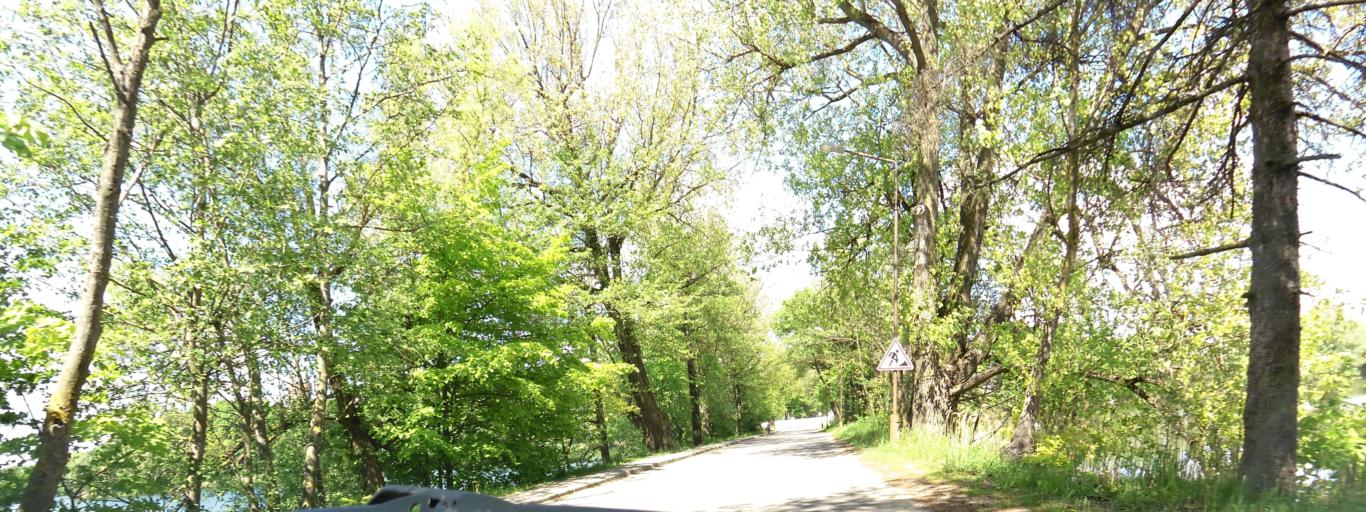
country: LT
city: Lentvaris
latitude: 54.6570
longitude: 25.0437
